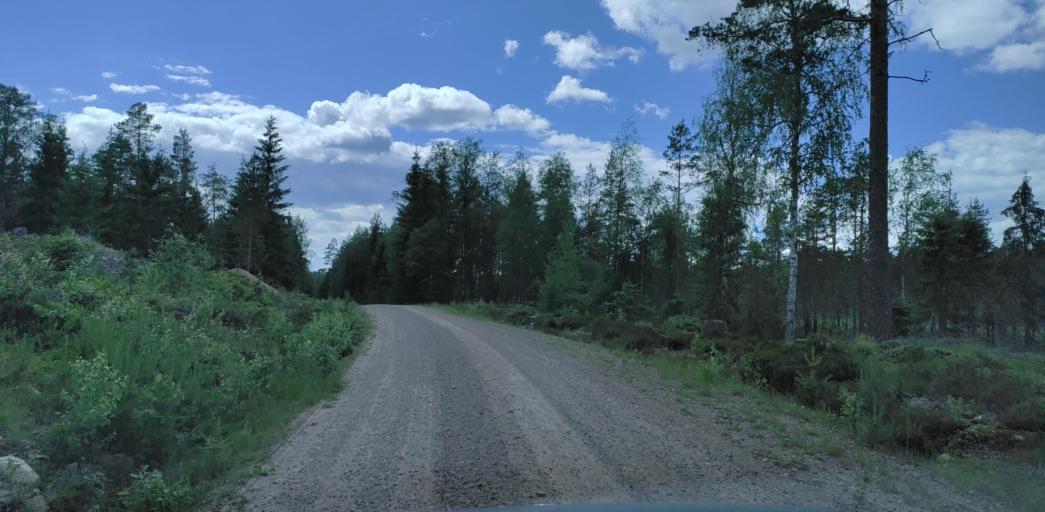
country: SE
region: Vaermland
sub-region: Hagfors Kommun
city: Ekshaerad
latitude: 60.0881
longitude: 13.3070
